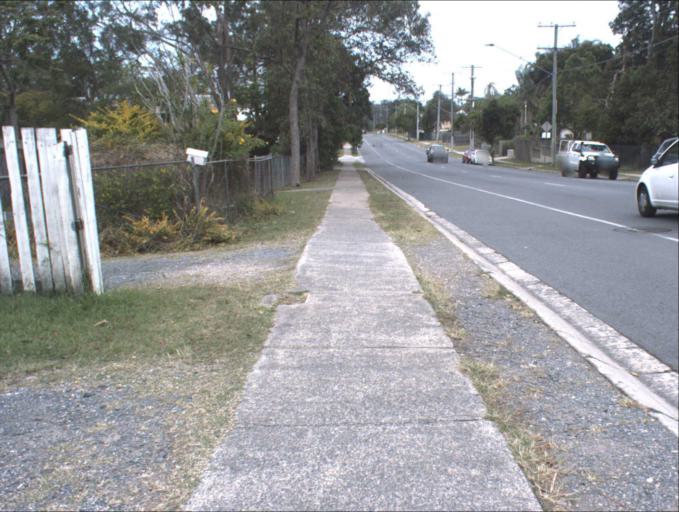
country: AU
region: Queensland
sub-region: Logan
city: Logan City
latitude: -27.6595
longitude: 153.1129
